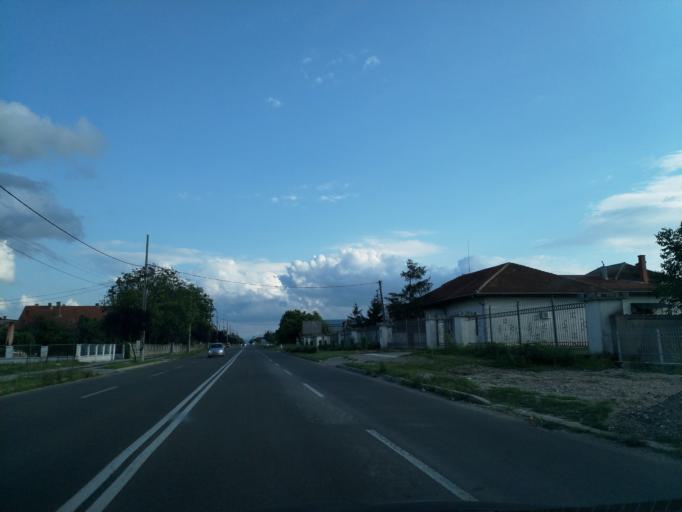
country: RS
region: Central Serbia
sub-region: Pomoravski Okrug
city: Paracin
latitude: 43.8380
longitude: 21.4156
